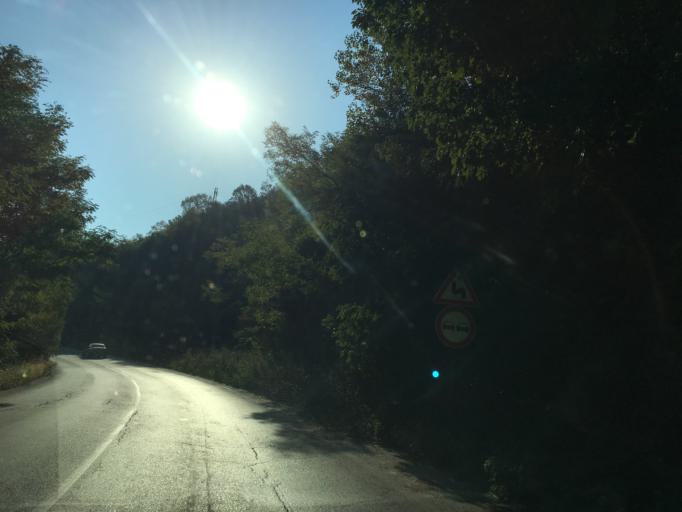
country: BG
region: Pazardzhik
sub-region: Obshtina Belovo
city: Belovo
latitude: 42.2446
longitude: 23.9306
